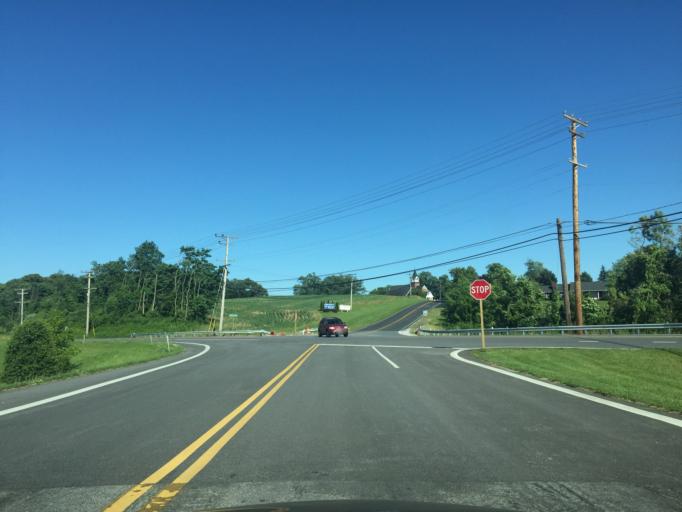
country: US
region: Maryland
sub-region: Carroll County
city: Westminster
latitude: 39.5992
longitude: -76.9380
